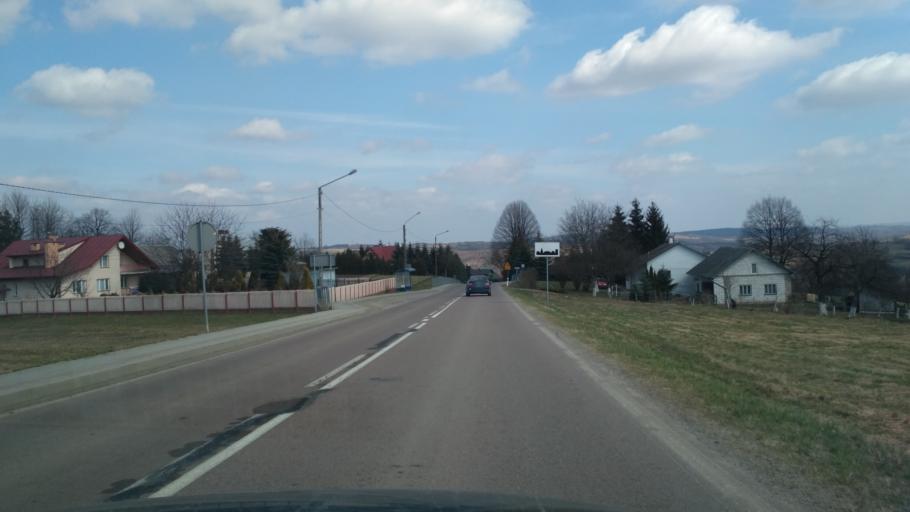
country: PL
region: Subcarpathian Voivodeship
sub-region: Powiat strzyzowski
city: Gwoznica Gorna
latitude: 49.8097
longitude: 22.0278
